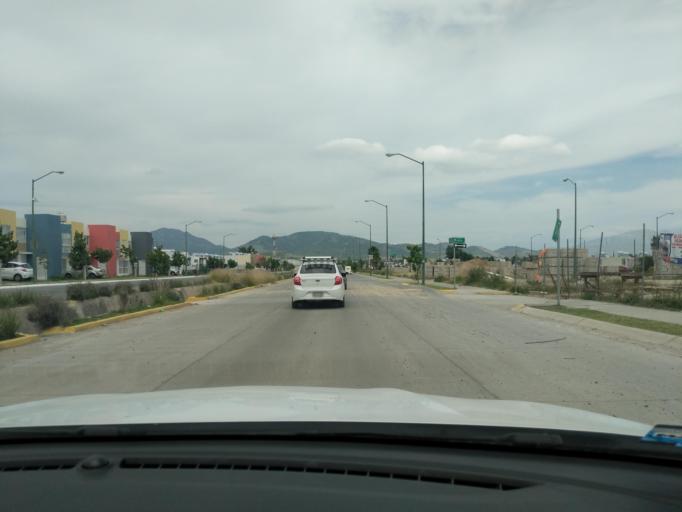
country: MX
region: Jalisco
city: Tesistan
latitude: 20.7870
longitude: -103.4890
